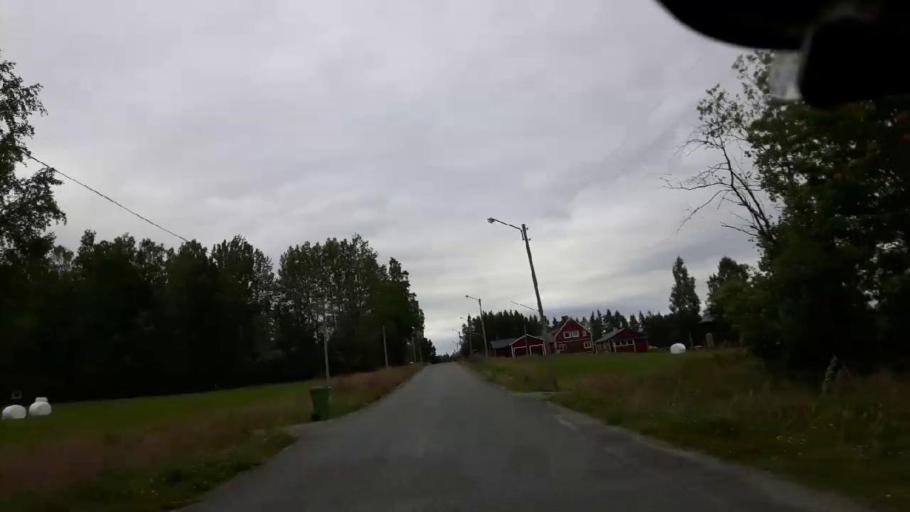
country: SE
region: Jaemtland
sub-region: Braecke Kommun
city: Braecke
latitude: 62.8397
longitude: 15.6805
